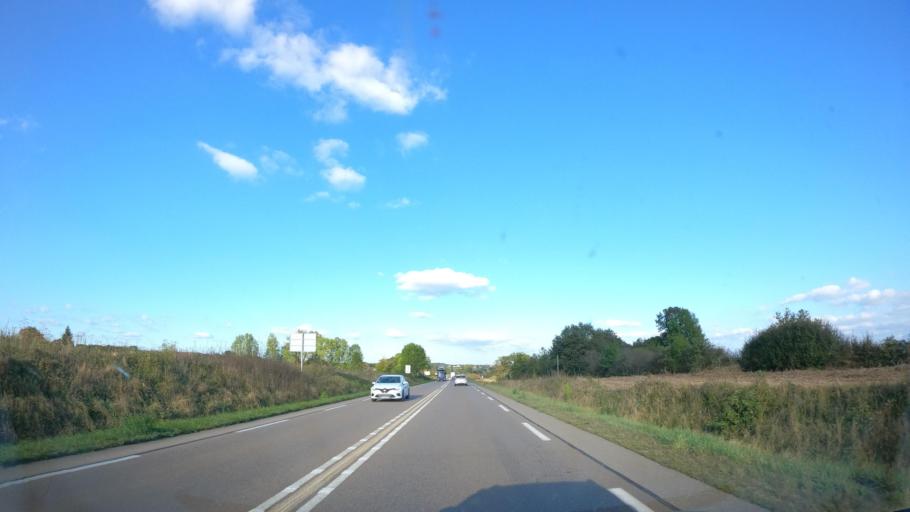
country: FR
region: Bourgogne
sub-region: Departement de Saone-et-Loire
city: Ciry-le-Noble
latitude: 46.6128
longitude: 4.2694
